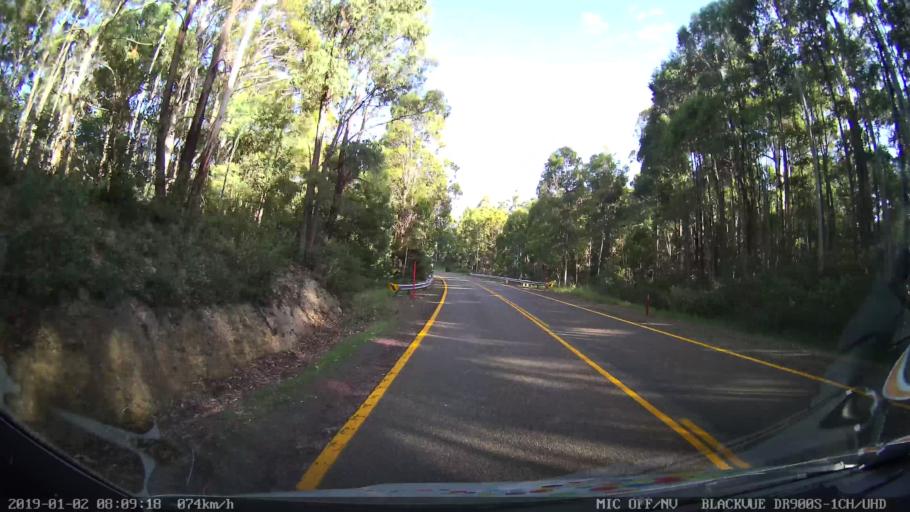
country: AU
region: New South Wales
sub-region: Tumut Shire
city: Tumut
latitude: -35.6082
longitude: 148.3806
